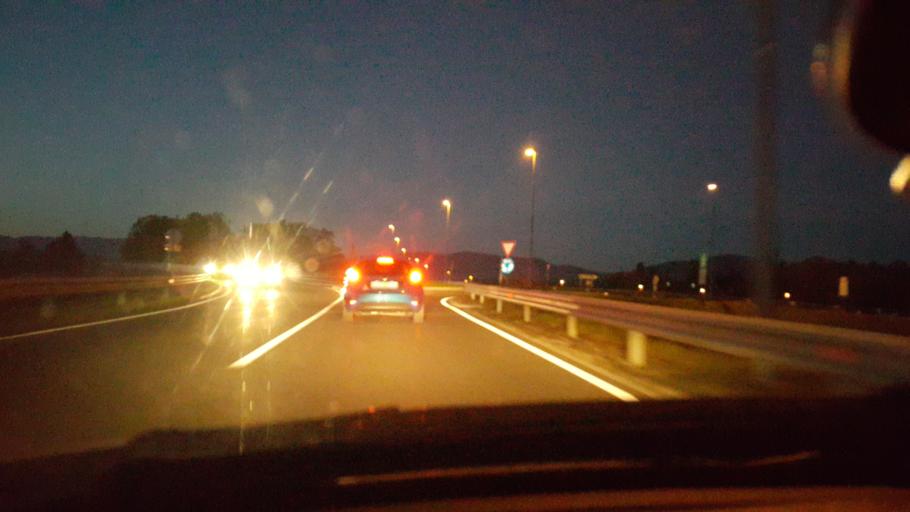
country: SI
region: Celje
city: Ljubecna
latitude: 46.2525
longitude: 15.3108
